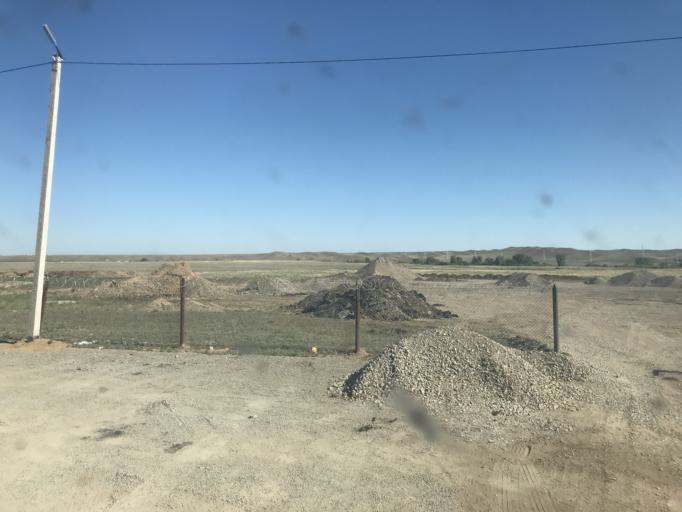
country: KZ
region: Aqtoebe
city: Aqtobe
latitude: 50.2966
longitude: 57.4764
